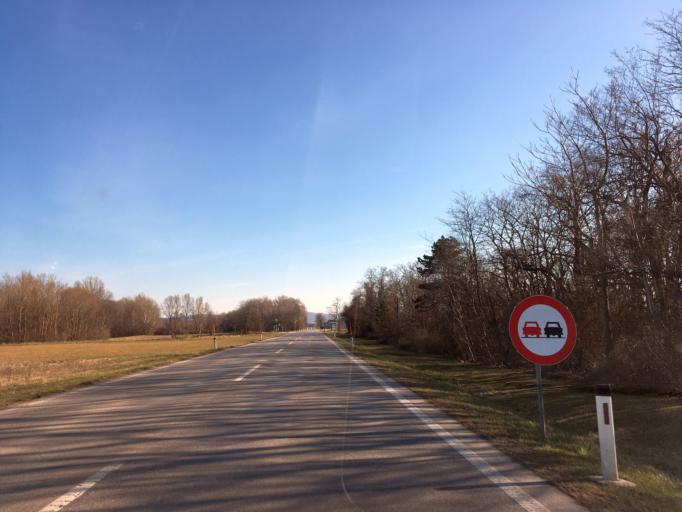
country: AT
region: Lower Austria
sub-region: Politischer Bezirk Baden
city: Ebreichsdorf
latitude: 47.9435
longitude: 16.4120
